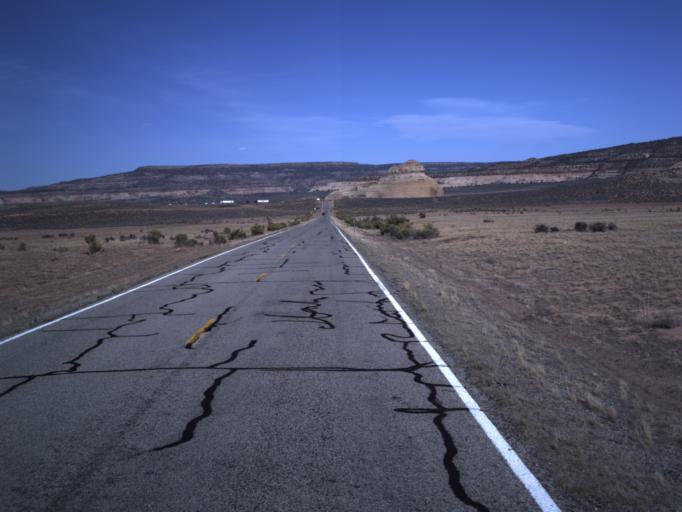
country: US
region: Utah
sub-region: San Juan County
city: Monticello
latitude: 38.0702
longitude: -109.3651
